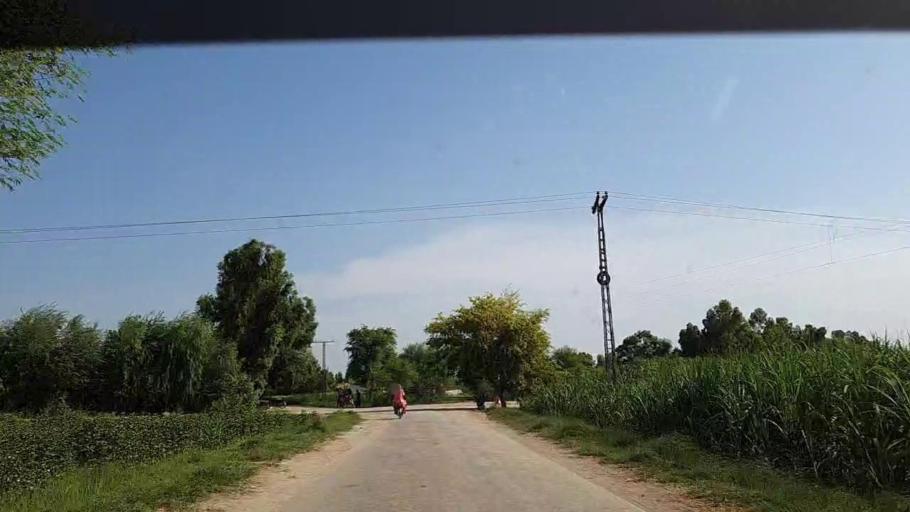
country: PK
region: Sindh
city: Adilpur
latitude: 27.9320
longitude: 69.2547
